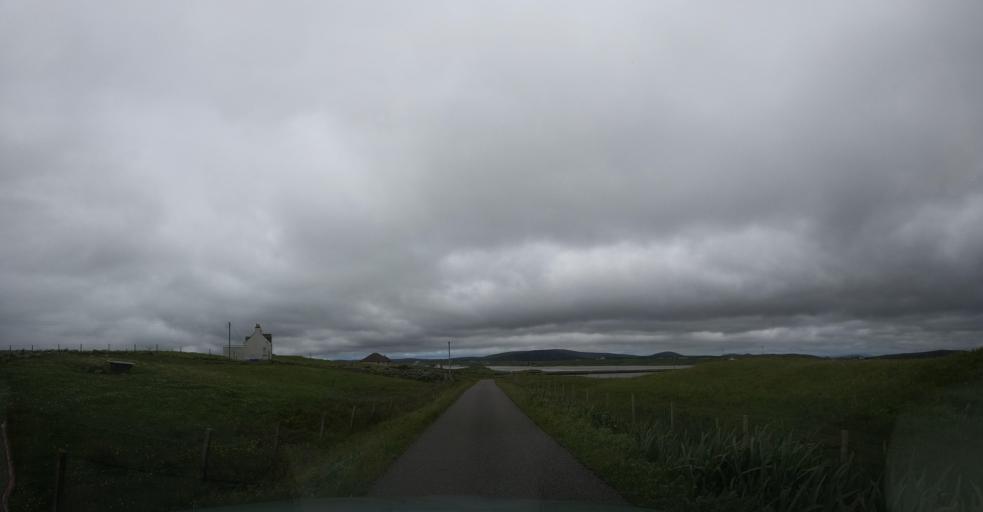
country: GB
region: Scotland
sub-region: Eilean Siar
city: Isle of North Uist
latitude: 57.5378
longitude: -7.3527
